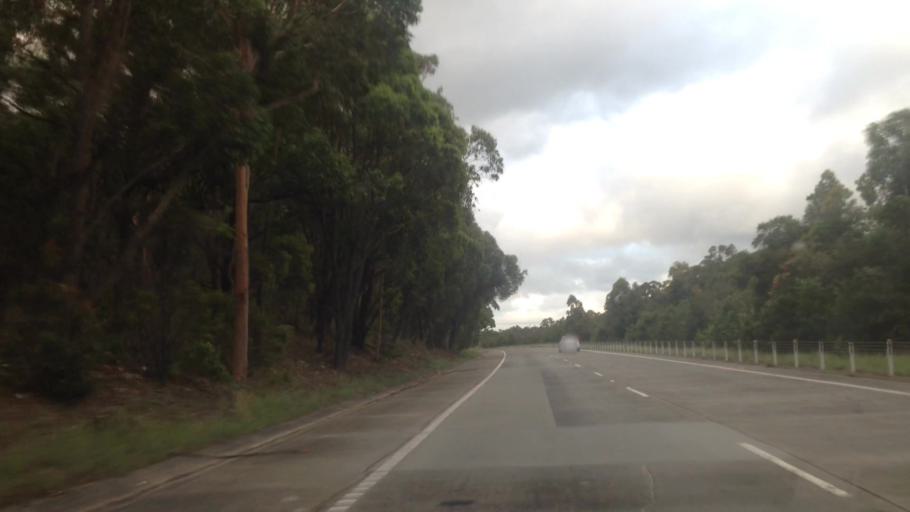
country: AU
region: New South Wales
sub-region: Wyong Shire
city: Charmhaven
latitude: -33.2000
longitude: 151.4624
